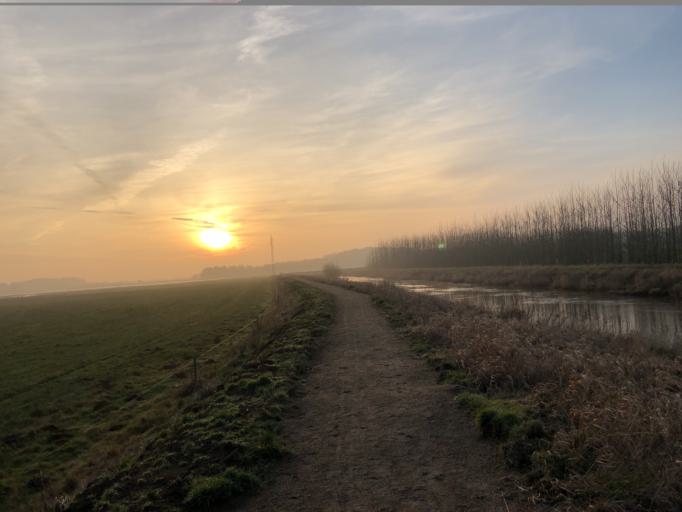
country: DK
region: Central Jutland
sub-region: Holstebro Kommune
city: Ulfborg
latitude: 56.3417
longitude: 8.3609
